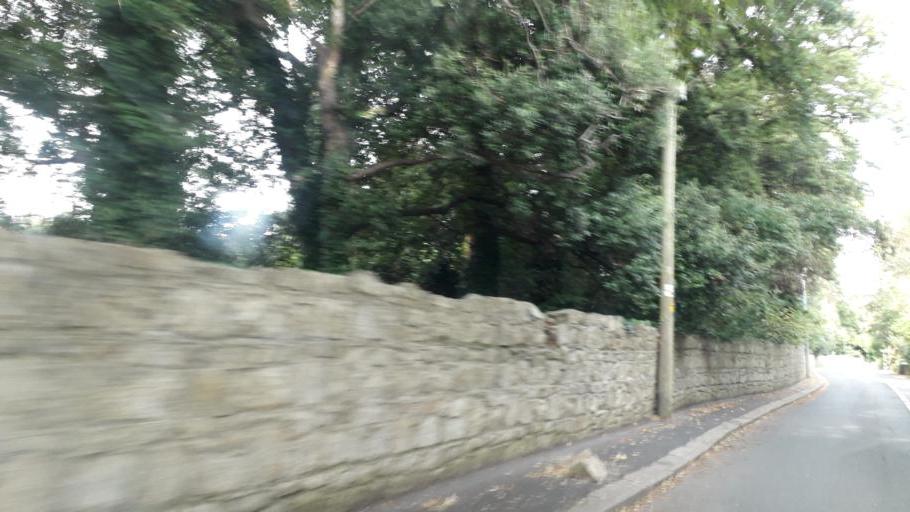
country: IE
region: Leinster
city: Cabinteely
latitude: 53.2554
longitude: -6.1539
